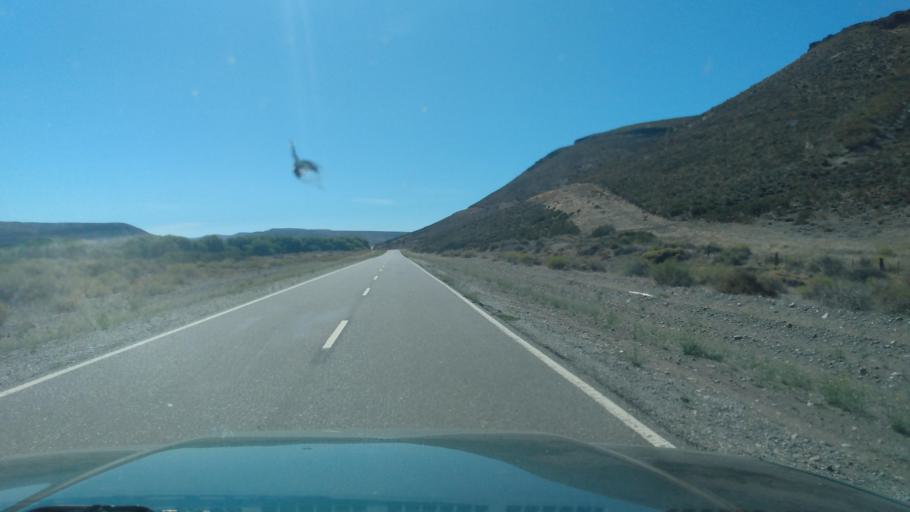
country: AR
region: Neuquen
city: Junin de los Andes
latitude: -40.1292
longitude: -70.7302
